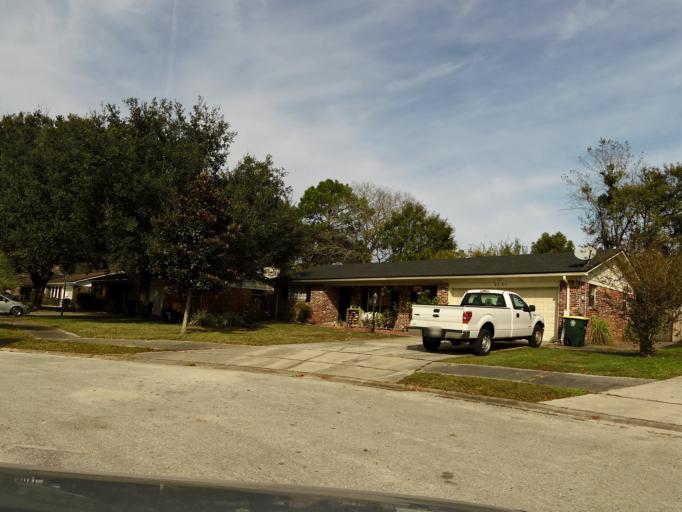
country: US
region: Florida
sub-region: Duval County
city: Jacksonville
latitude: 30.2266
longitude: -81.5940
